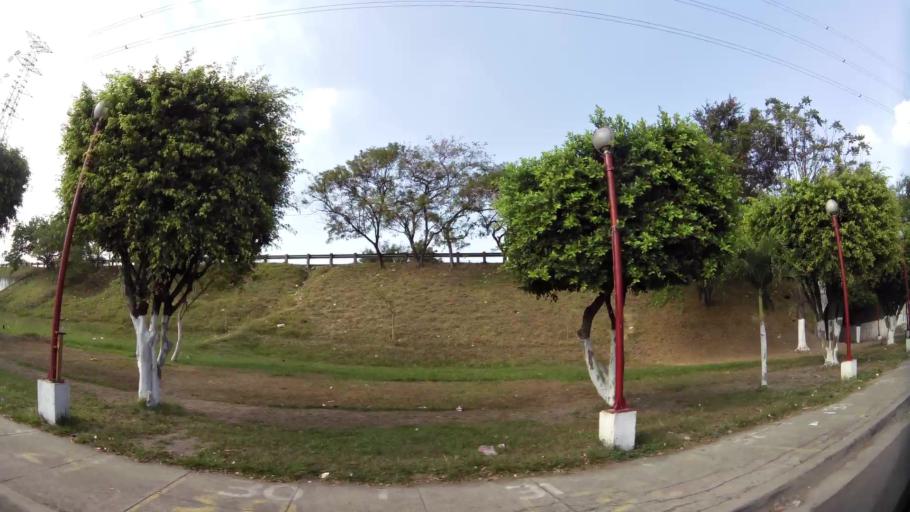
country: SV
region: San Salvador
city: Soyapango
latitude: 13.7157
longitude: -89.1410
